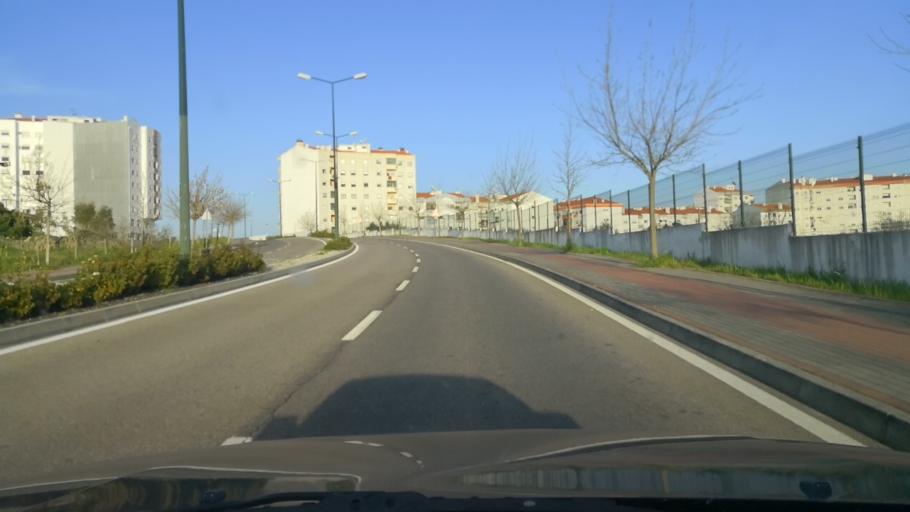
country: PT
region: Castelo Branco
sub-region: Castelo Branco
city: Castelo Branco
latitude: 39.8171
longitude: -7.4889
